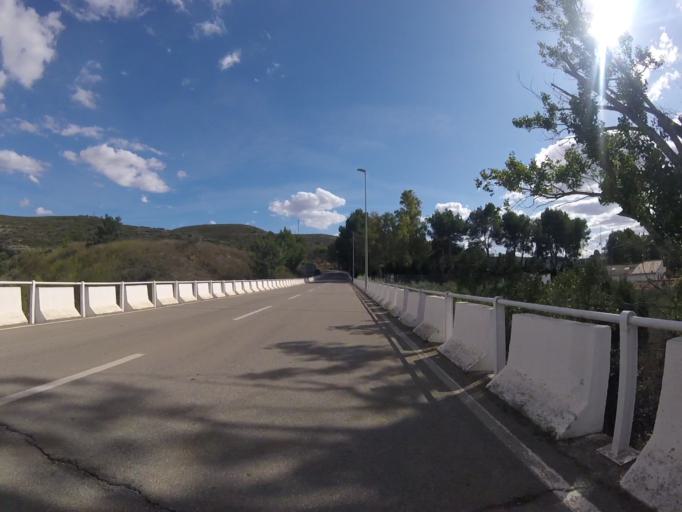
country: ES
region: Valencia
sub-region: Provincia de Castello
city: Cuevas de Vinroma
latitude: 40.3148
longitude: 0.1239
